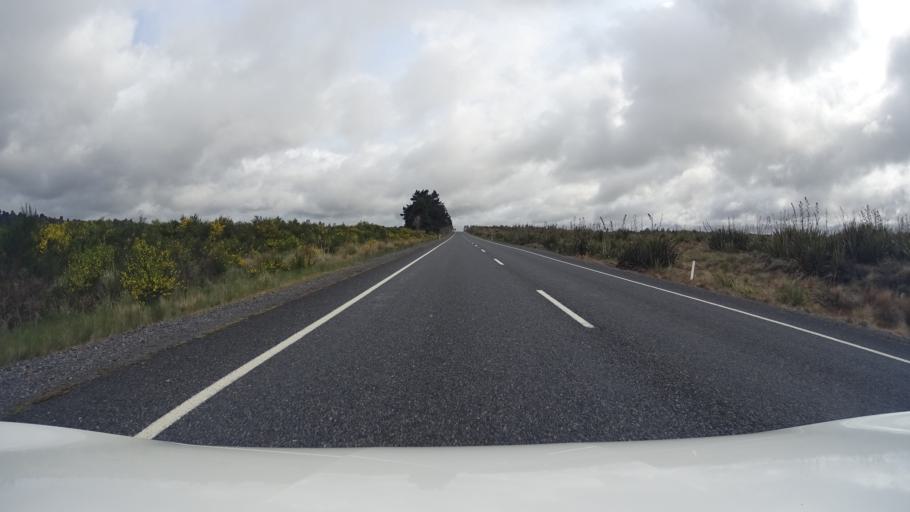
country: NZ
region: Manawatu-Wanganui
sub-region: Ruapehu District
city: Waiouru
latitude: -39.1839
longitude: 175.4021
